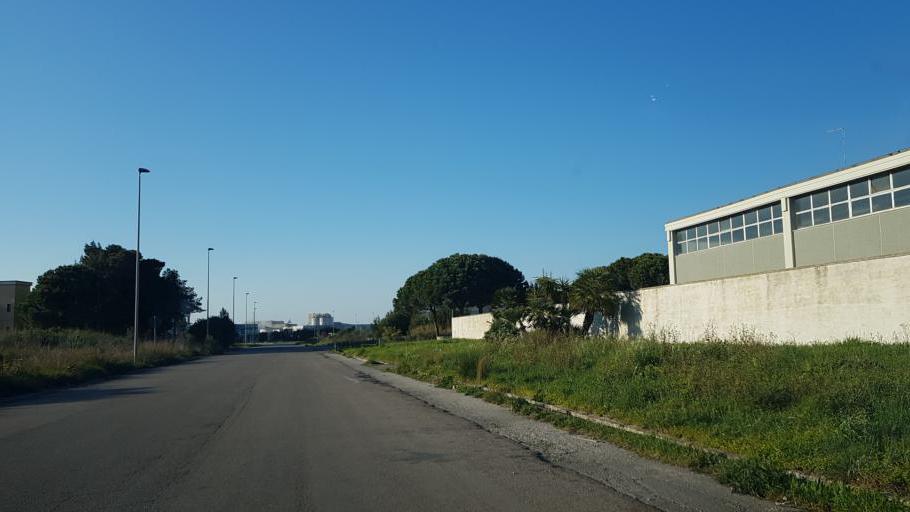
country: IT
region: Apulia
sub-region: Provincia di Brindisi
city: La Rosa
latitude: 40.6282
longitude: 17.9666
